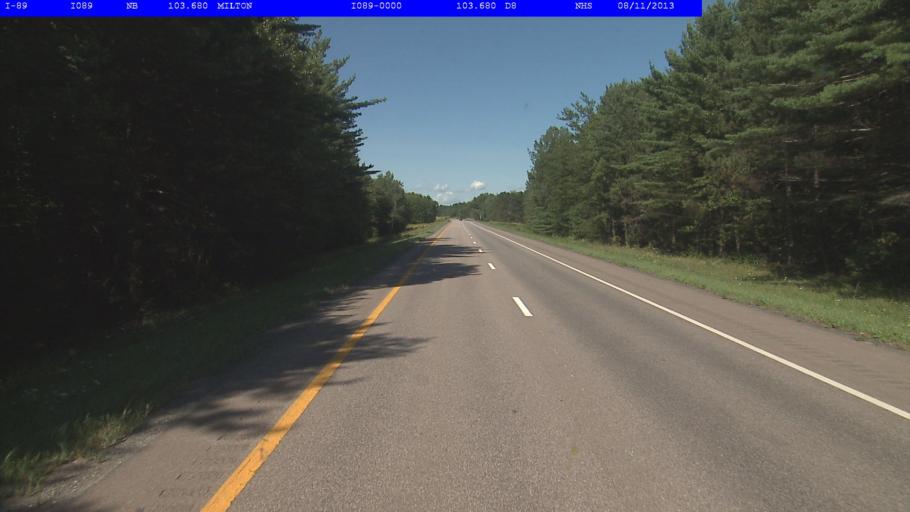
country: US
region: Vermont
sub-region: Chittenden County
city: Milton
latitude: 44.6661
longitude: -73.1354
